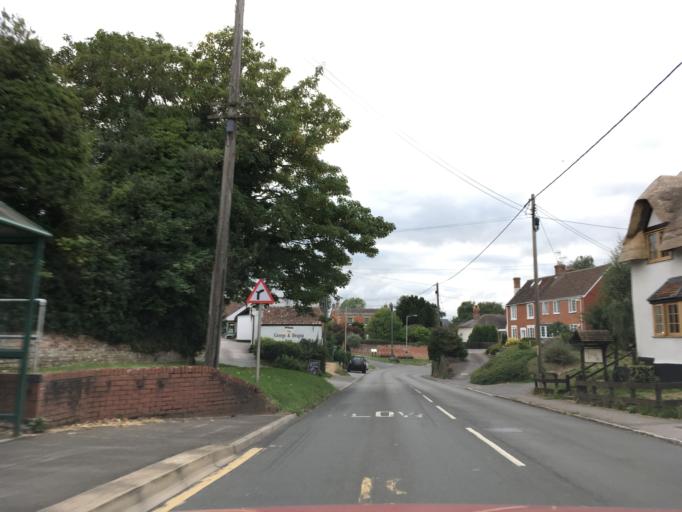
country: GB
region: England
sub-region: Wiltshire
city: Devizes
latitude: 51.3635
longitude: -2.0315
